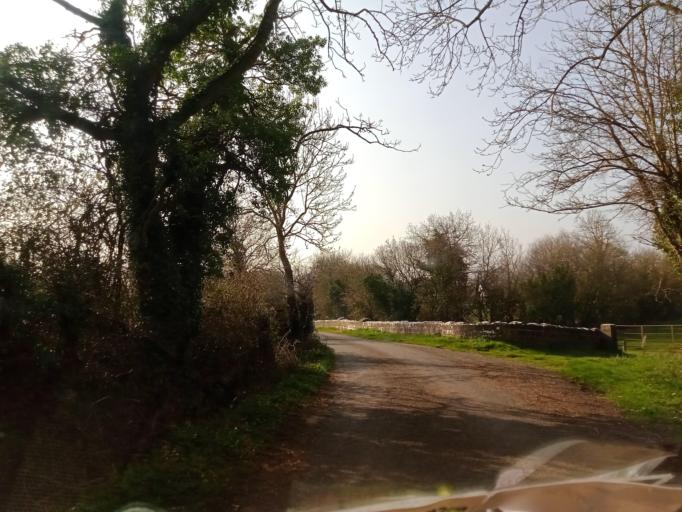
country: IE
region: Leinster
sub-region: Kilkenny
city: Callan
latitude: 52.5284
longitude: -7.3999
